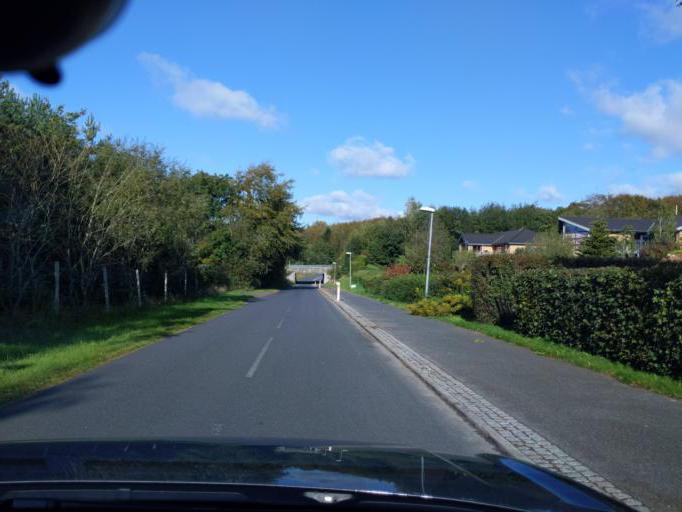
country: DK
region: Central Jutland
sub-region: Viborg Kommune
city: Viborg
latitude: 56.4712
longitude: 9.4369
